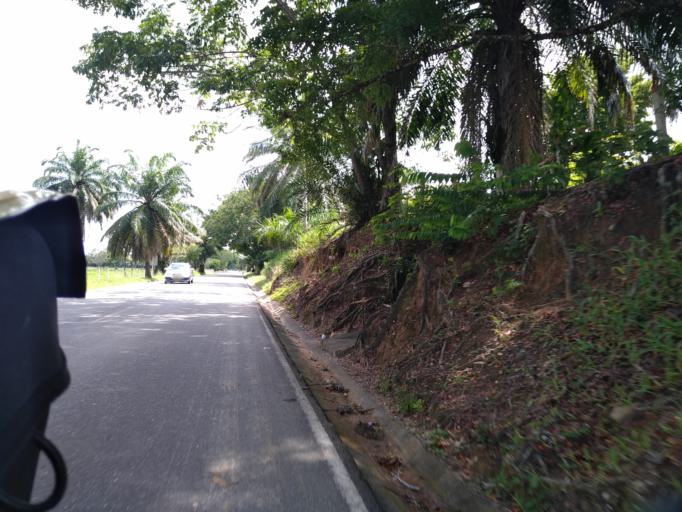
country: CO
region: Santander
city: Cimitarra
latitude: 6.4460
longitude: -74.0225
